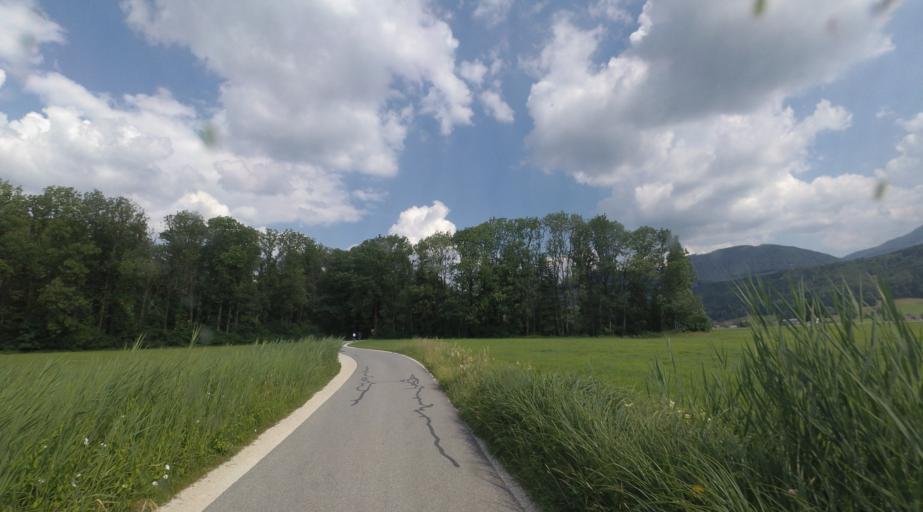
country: DE
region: Bavaria
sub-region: Upper Bavaria
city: Bergen
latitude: 47.8101
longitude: 12.5698
